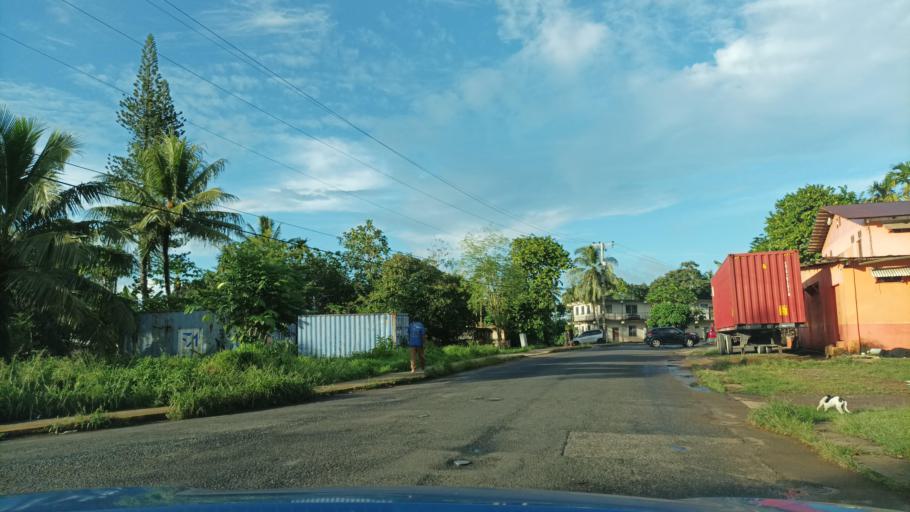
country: FM
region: Pohnpei
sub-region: Kolonia Municipality
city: Kolonia
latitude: 6.9609
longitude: 158.2089
